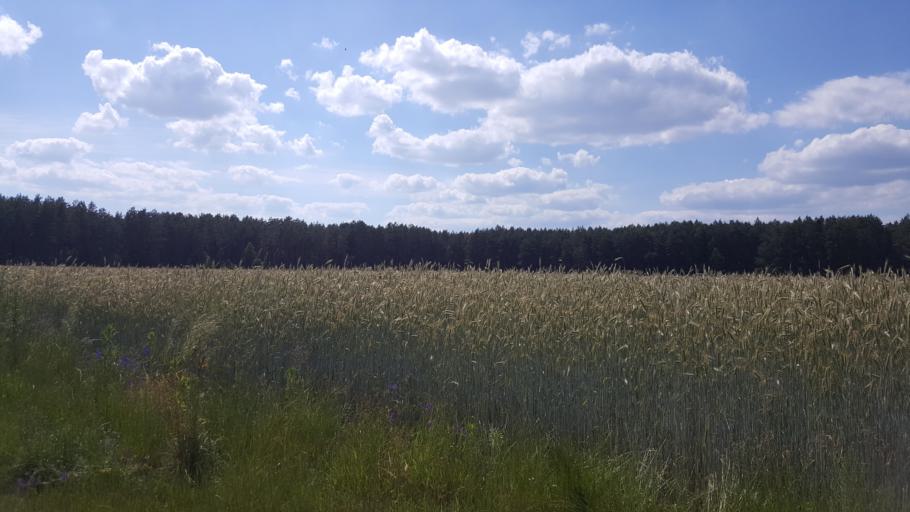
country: BY
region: Brest
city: Kamyanyuki
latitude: 52.5062
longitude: 23.6881
